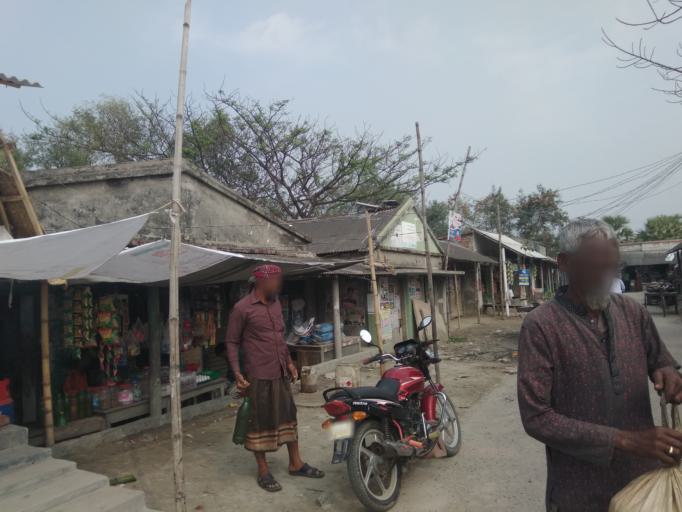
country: IN
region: West Bengal
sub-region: North 24 Parganas
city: Taki
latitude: 22.3469
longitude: 89.2083
